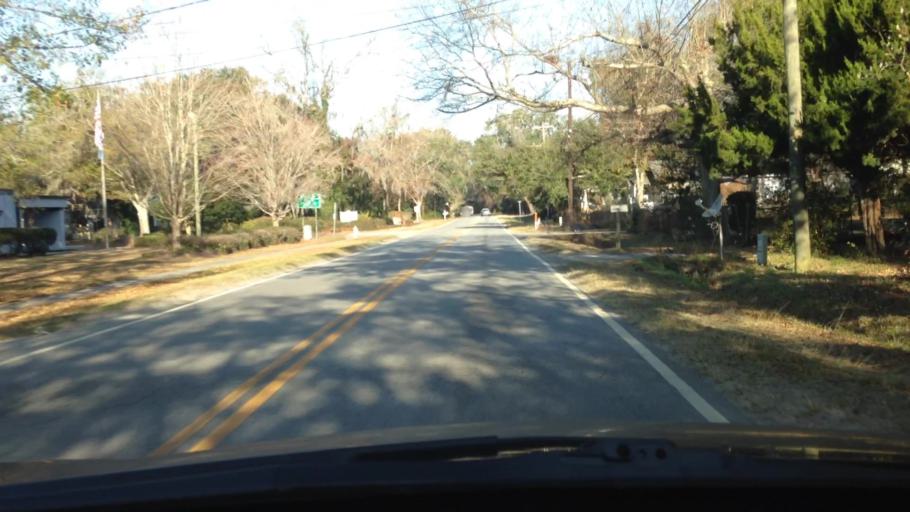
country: US
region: South Carolina
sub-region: Charleston County
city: Charleston
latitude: 32.7467
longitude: -79.9872
